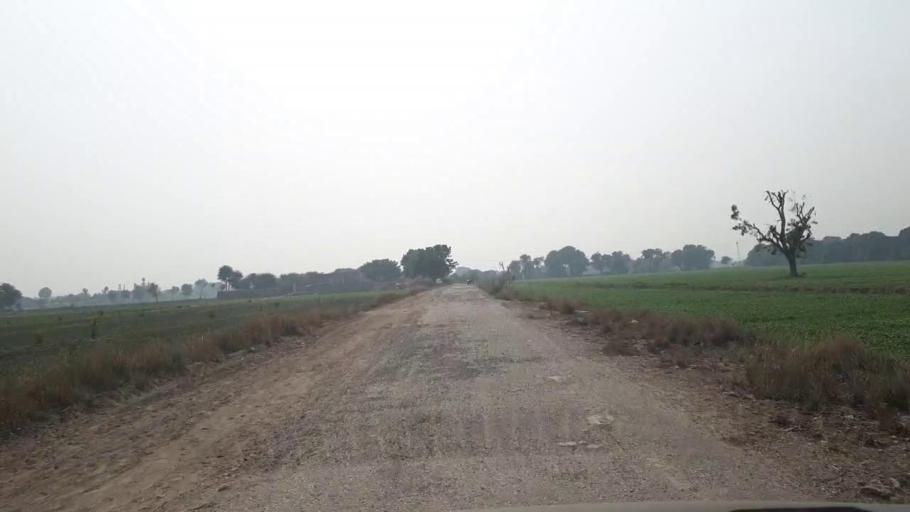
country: PK
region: Sindh
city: Bhit Shah
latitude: 25.8541
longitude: 68.4992
